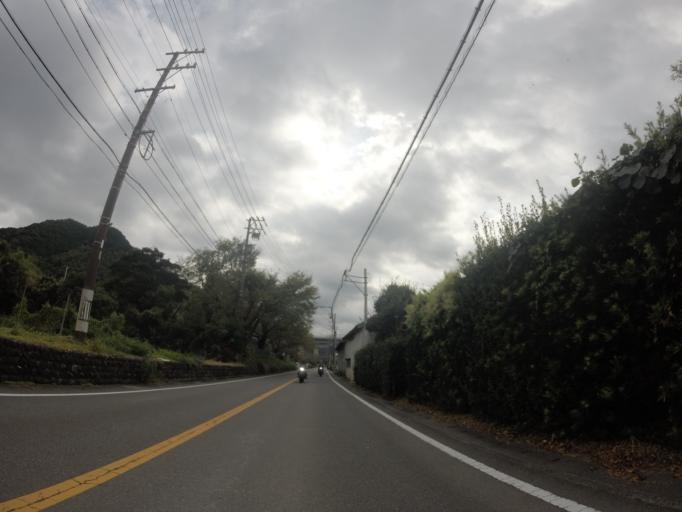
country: JP
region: Shizuoka
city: Fujieda
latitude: 34.8902
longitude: 138.2160
